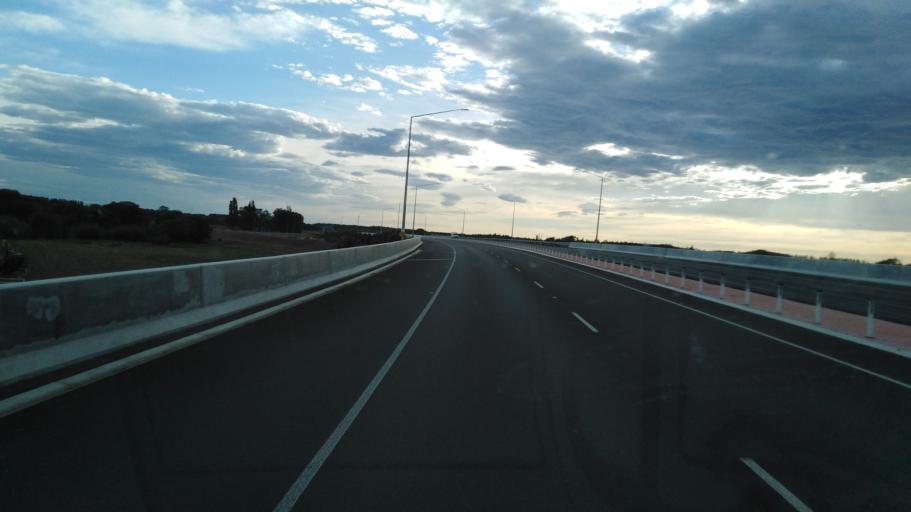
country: NZ
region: Canterbury
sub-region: Waimakariri District
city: Kaiapoi
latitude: -43.4362
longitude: 172.6346
